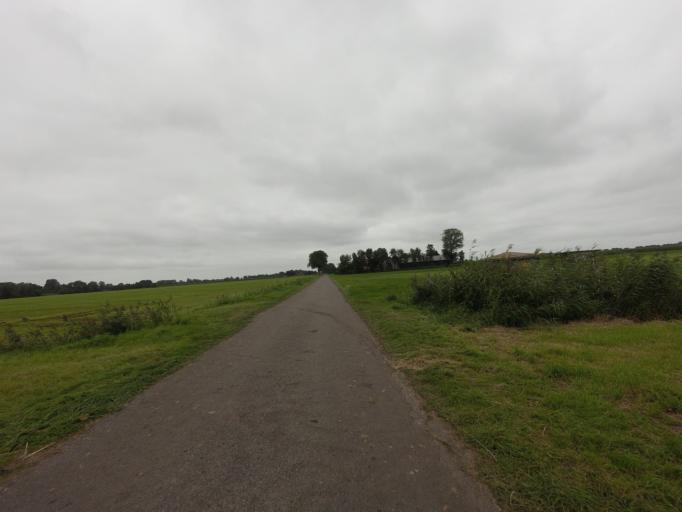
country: NL
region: Overijssel
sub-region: Gemeente Steenwijkerland
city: Blokzijl
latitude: 52.7360
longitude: 6.0098
